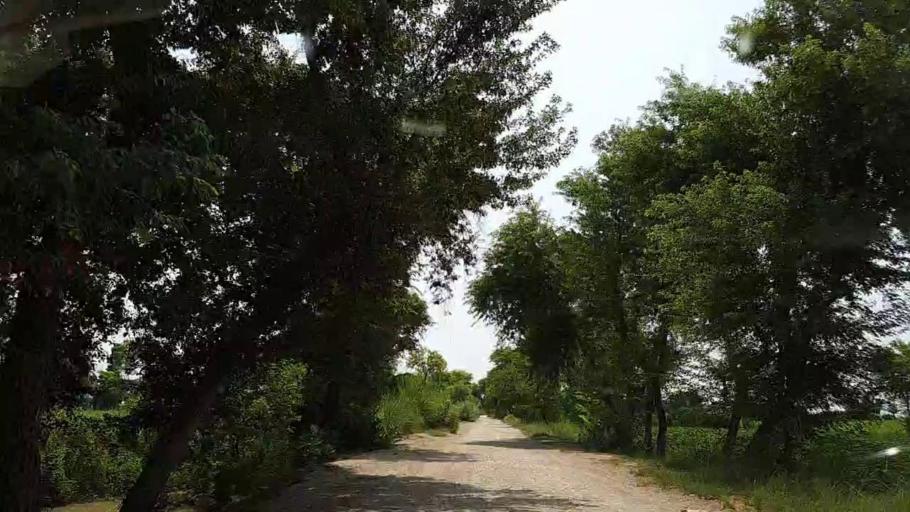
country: PK
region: Sindh
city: Adilpur
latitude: 27.9334
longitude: 69.3917
